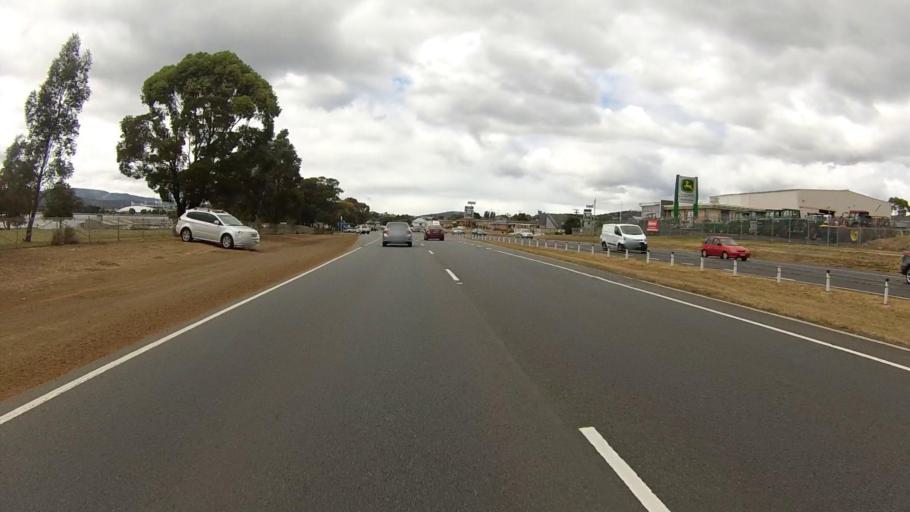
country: AU
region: Tasmania
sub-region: Glenorchy
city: Glenorchy
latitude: -42.8211
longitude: 147.2658
